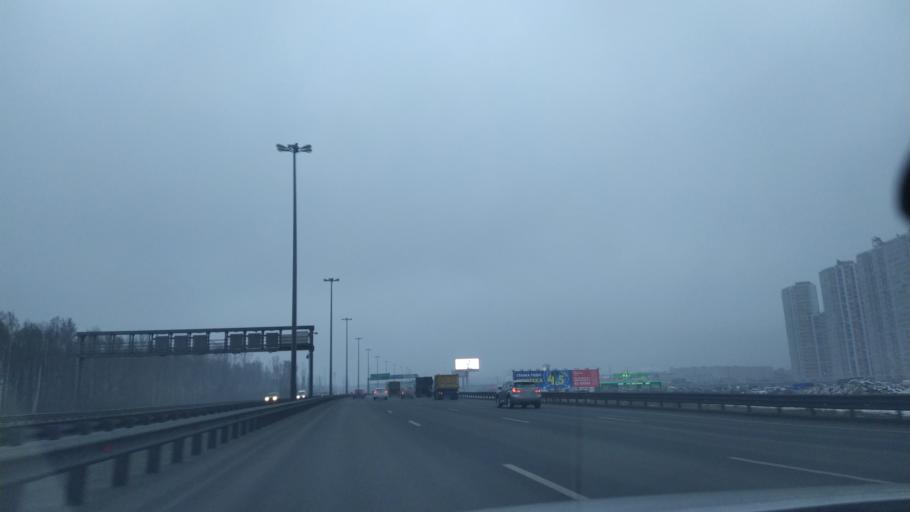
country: RU
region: Leningrad
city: Rybatskoye
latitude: 59.9030
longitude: 30.5263
